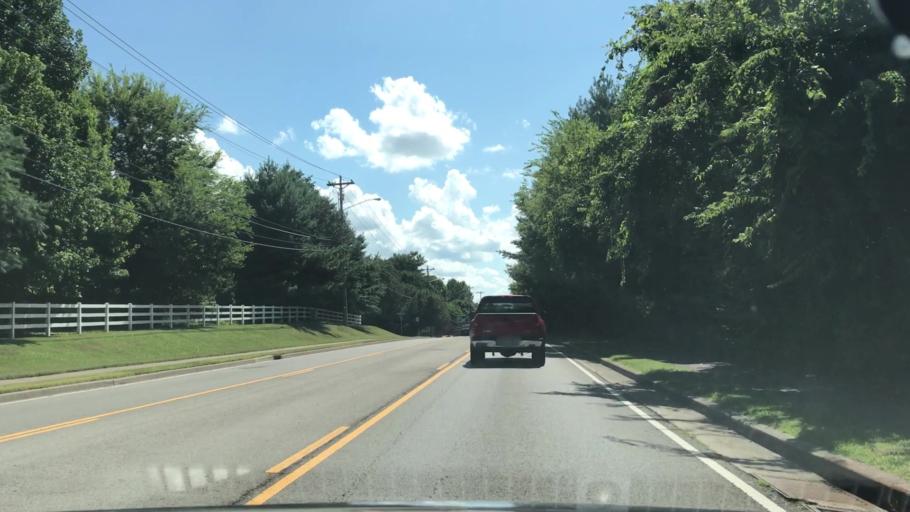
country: US
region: Tennessee
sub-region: Williamson County
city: Franklin
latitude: 35.9290
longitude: -86.8382
